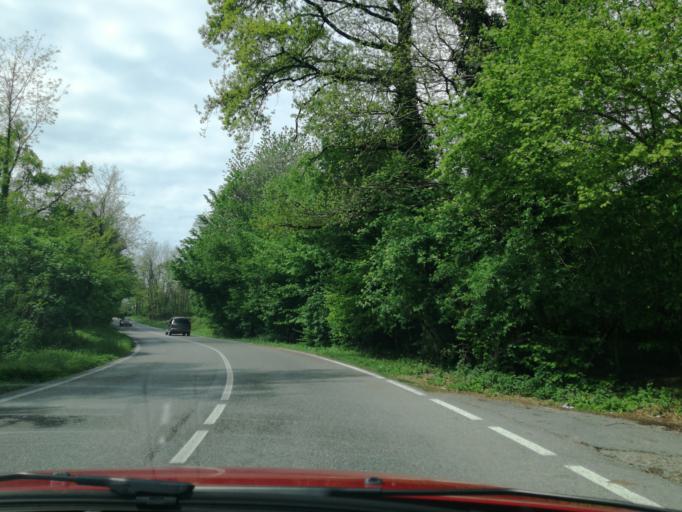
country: IT
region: Lombardy
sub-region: Provincia di Lecco
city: Garbagnate
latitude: 45.7643
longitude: 9.3010
